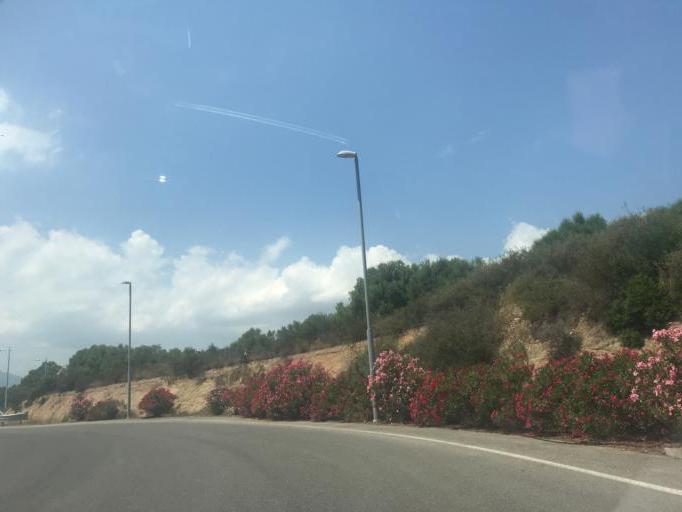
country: IT
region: Sardinia
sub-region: Provincia di Olbia-Tempio
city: Olbia
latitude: 40.9022
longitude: 9.5080
